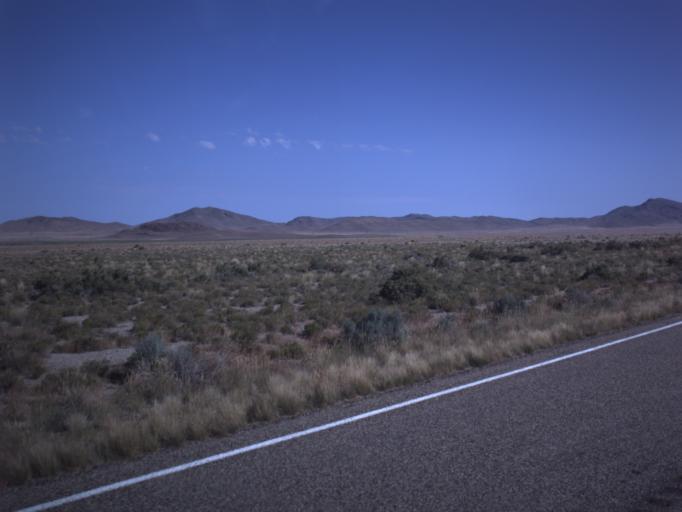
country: US
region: Utah
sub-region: Beaver County
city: Milford
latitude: 38.6580
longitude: -112.9817
